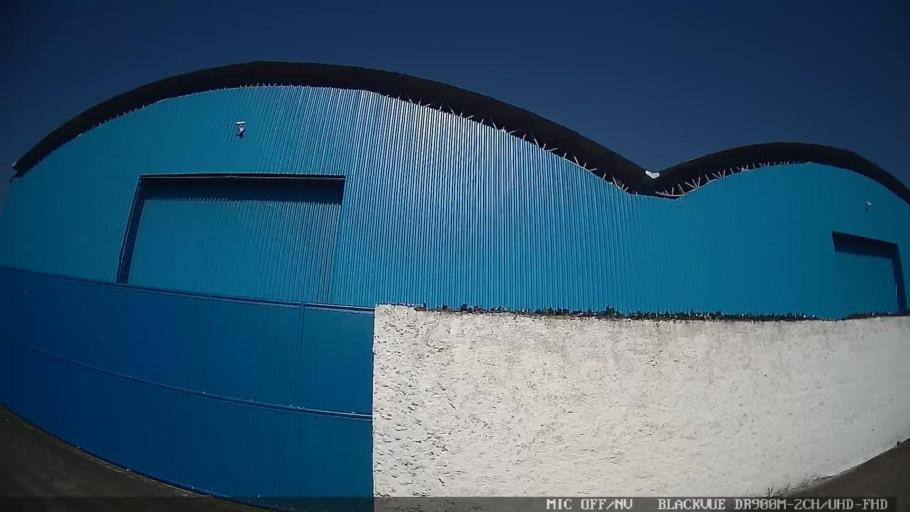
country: BR
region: Sao Paulo
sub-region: Guaruja
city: Guaruja
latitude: -24.0010
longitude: -46.2913
